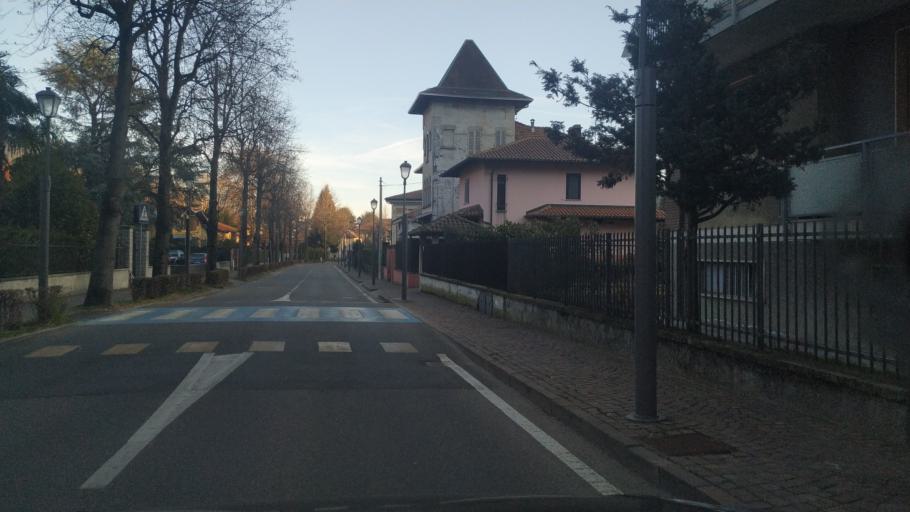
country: IT
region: Piedmont
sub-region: Provincia di Vercelli
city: Borgosesia
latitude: 45.7237
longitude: 8.2651
